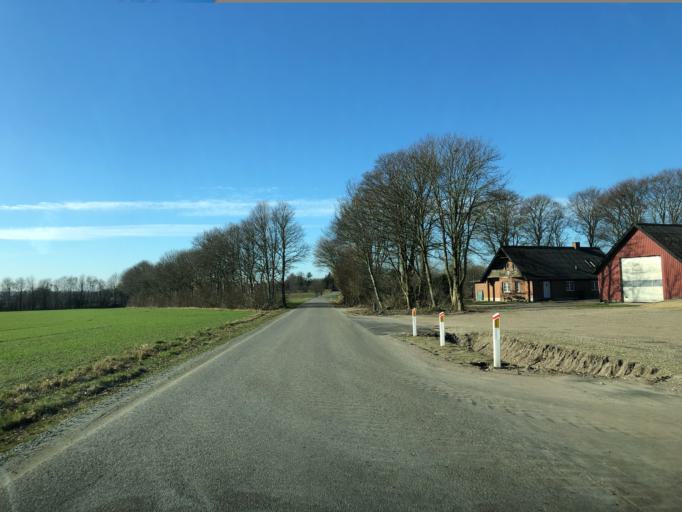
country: DK
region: Central Jutland
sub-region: Ikast-Brande Kommune
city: Bording Kirkeby
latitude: 56.1554
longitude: 9.2419
